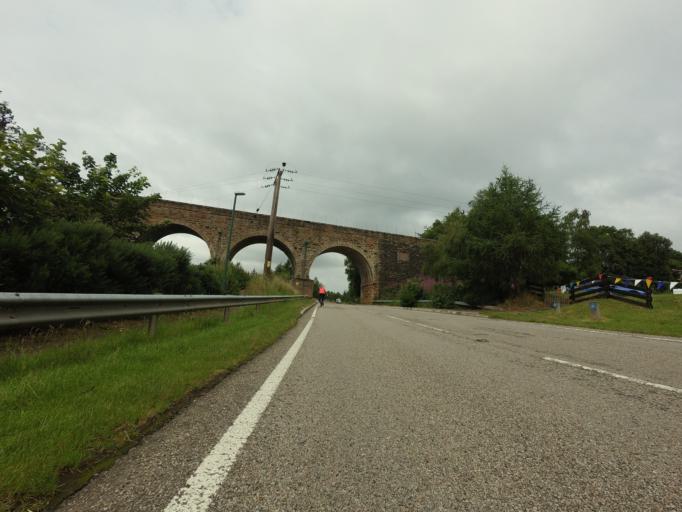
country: GB
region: Scotland
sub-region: Highland
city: Evanton
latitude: 57.9240
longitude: -4.4000
